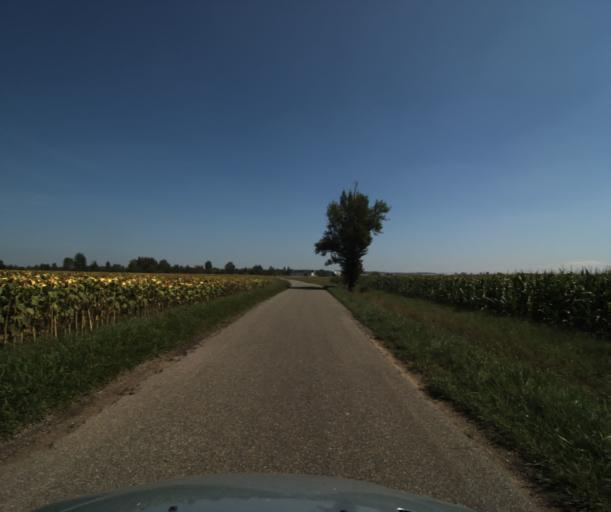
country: FR
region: Midi-Pyrenees
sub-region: Departement de la Haute-Garonne
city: Labastidette
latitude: 43.4545
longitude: 1.2623
